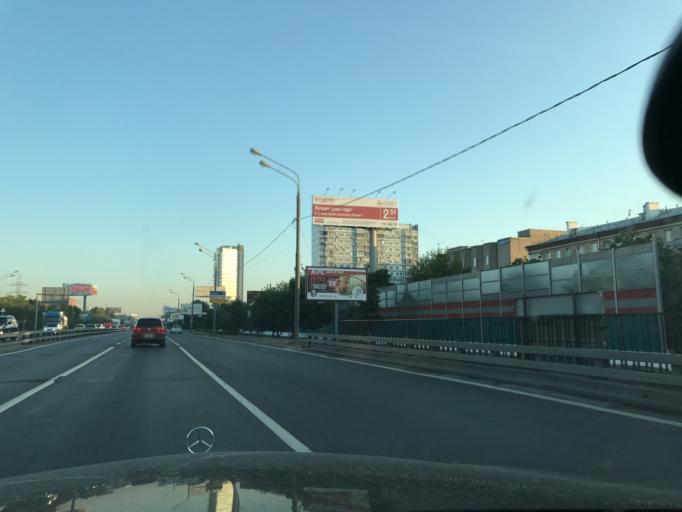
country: RU
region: Moscow
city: Khimki
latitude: 55.8900
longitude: 37.4351
